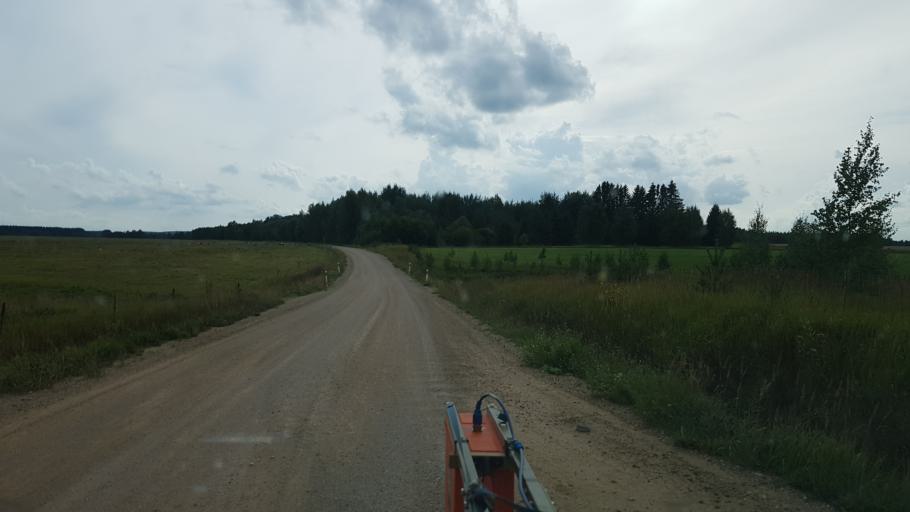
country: RU
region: Pskov
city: Pechory
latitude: 57.7903
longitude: 27.4772
